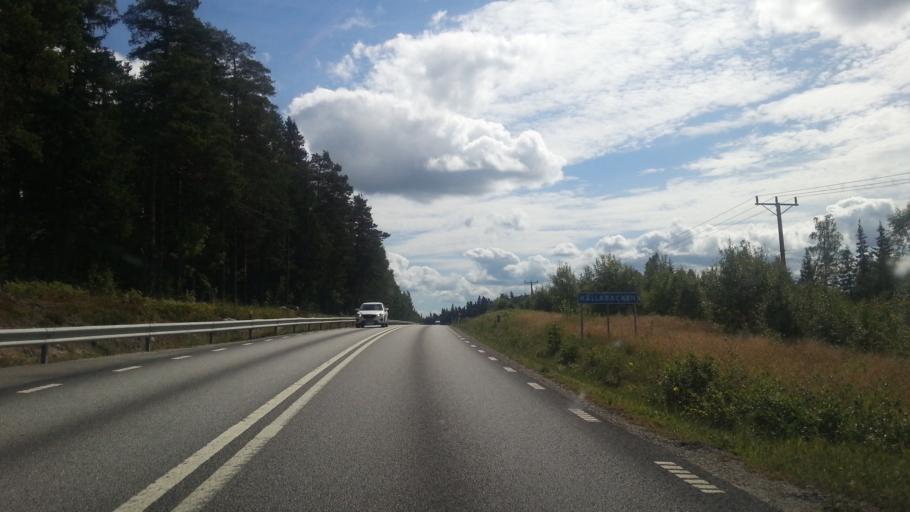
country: SE
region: OErebro
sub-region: Lindesbergs Kommun
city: Stora
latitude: 59.6471
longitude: 15.1299
